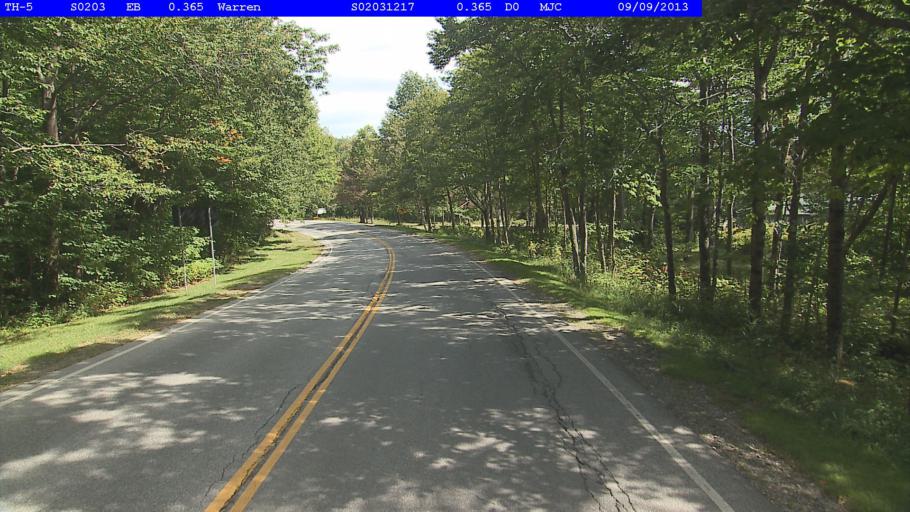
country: US
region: Vermont
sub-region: Addison County
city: Bristol
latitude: 44.1369
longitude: -72.8883
